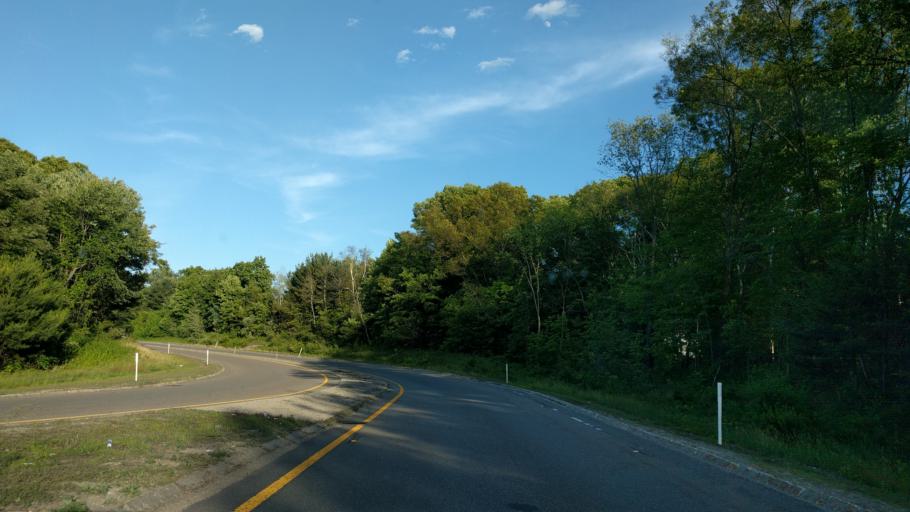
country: US
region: Massachusetts
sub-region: Middlesex County
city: Hudson
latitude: 42.3613
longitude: -71.5926
